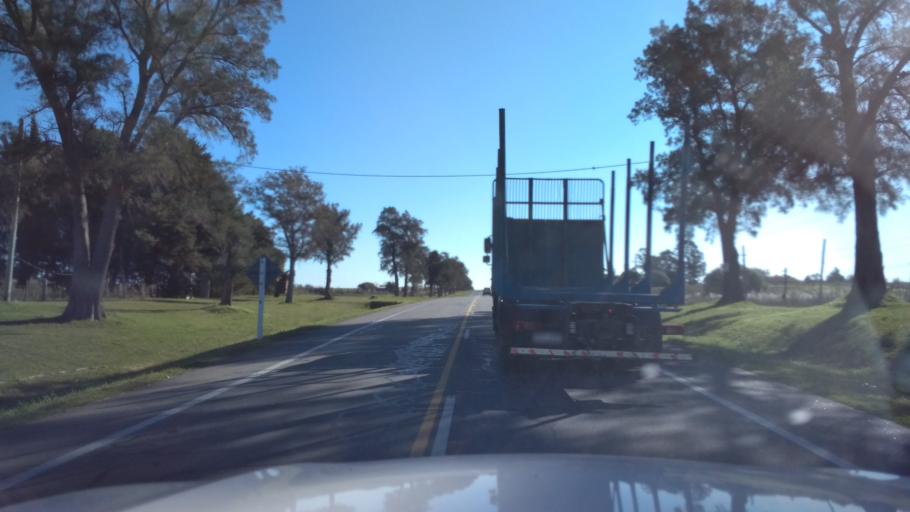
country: UY
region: Canelones
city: San Jacinto
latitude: -34.5406
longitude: -55.8934
